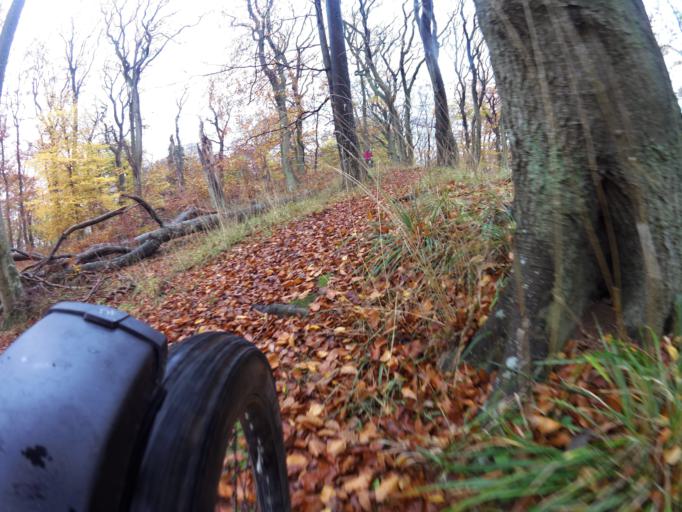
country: PL
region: Pomeranian Voivodeship
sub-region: Powiat pucki
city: Krokowa
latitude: 54.7576
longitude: 18.0859
